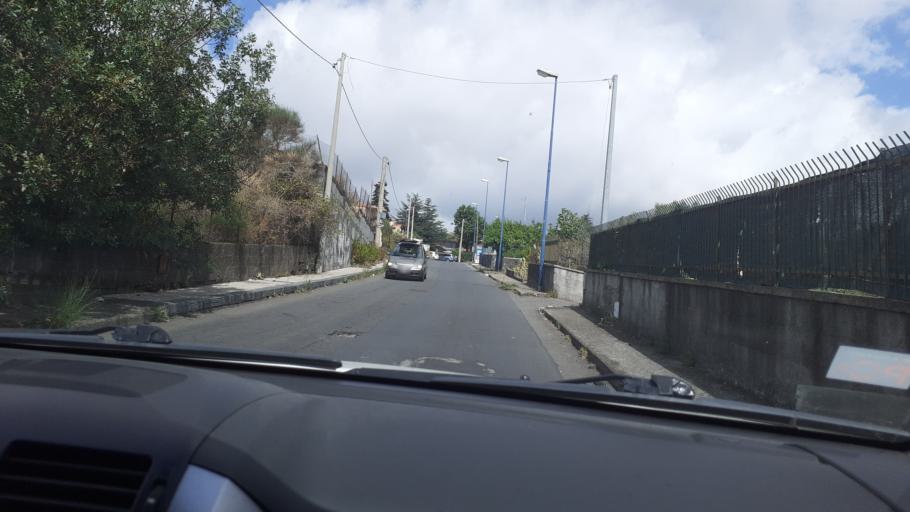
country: IT
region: Sicily
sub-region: Catania
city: Pedara
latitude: 37.6107
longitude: 15.0580
